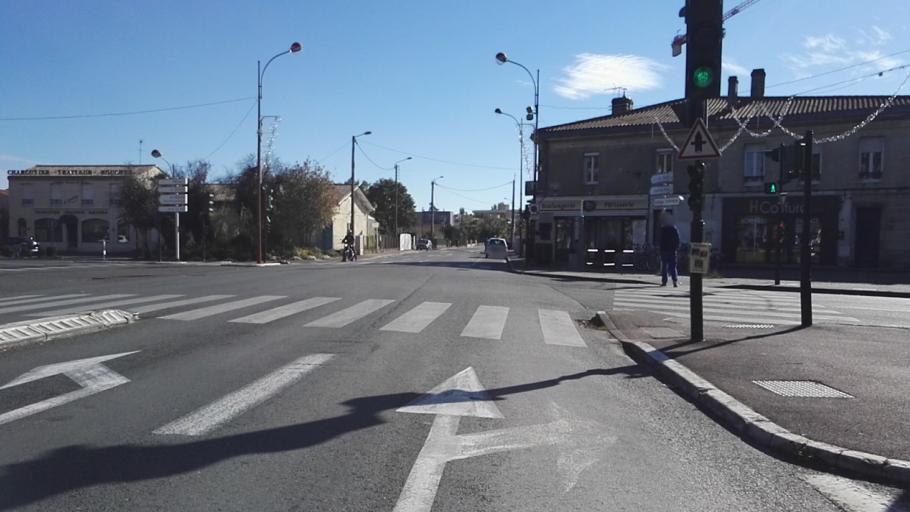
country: FR
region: Aquitaine
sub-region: Departement de la Gironde
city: Merignac
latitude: 44.8512
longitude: -0.6448
